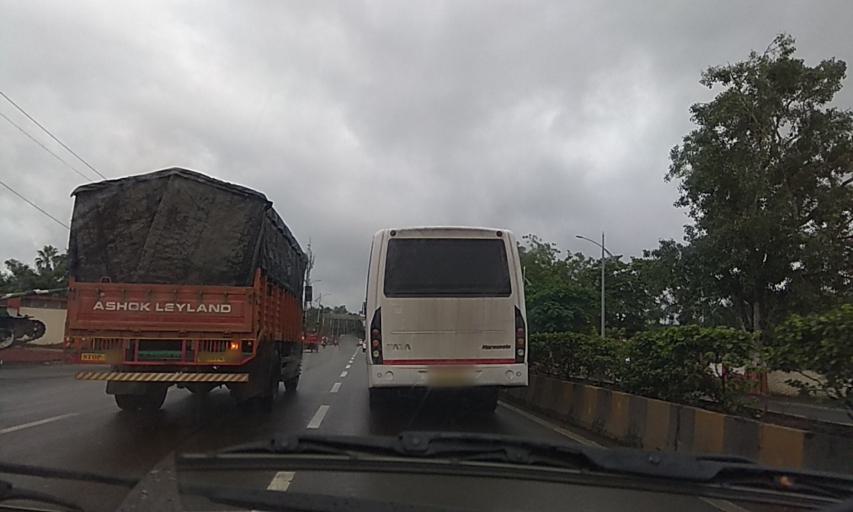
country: IN
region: Maharashtra
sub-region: Pune Division
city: Khadki
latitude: 18.5516
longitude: 73.8668
